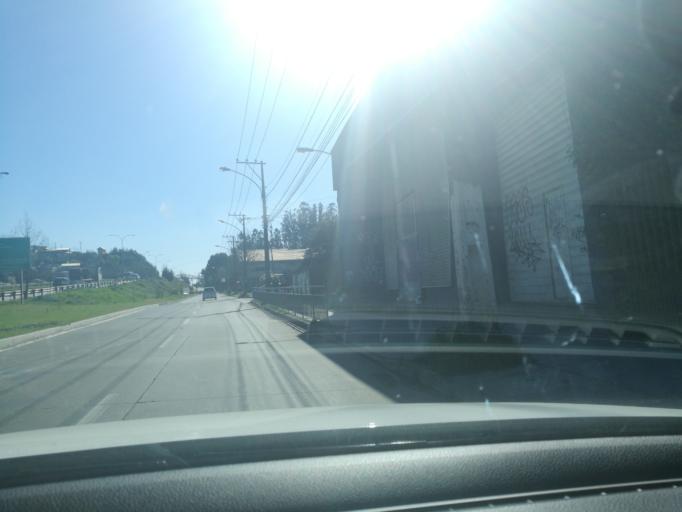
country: CL
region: Biobio
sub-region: Provincia de Concepcion
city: Concepcion
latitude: -36.8087
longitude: -73.0304
